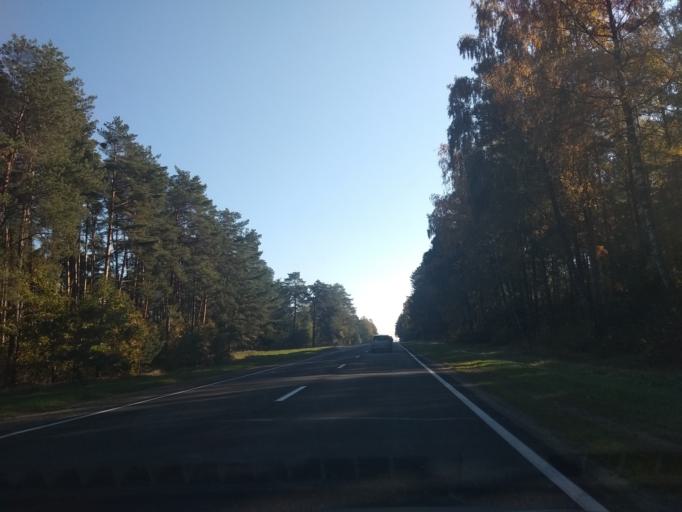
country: BY
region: Grodnenskaya
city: Zel'va
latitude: 53.1327
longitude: 25.0016
